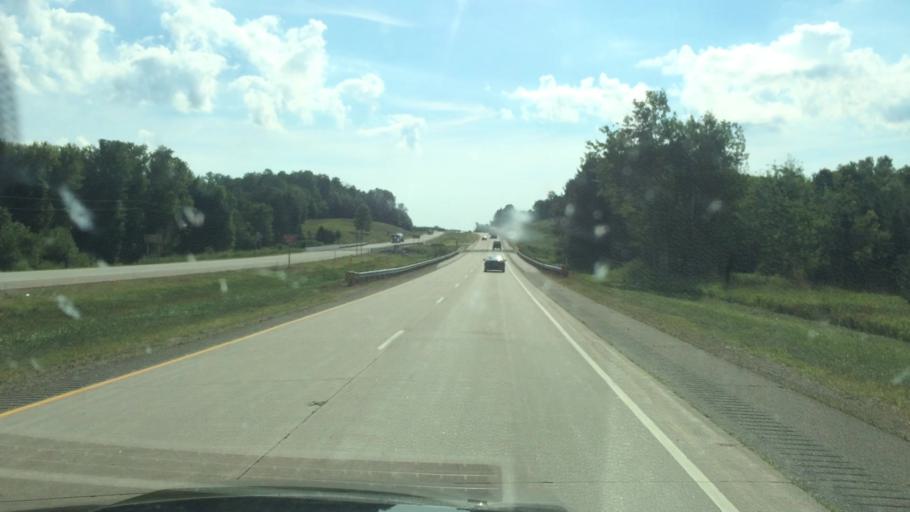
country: US
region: Wisconsin
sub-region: Shawano County
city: Wittenberg
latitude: 44.8036
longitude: -89.0191
